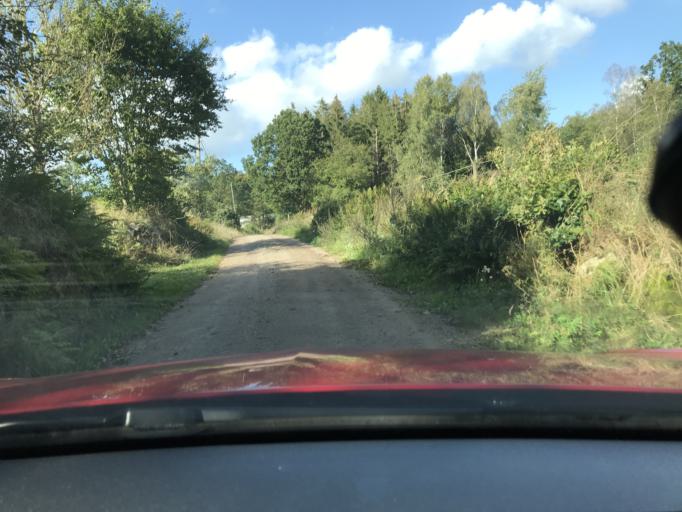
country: SE
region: Skane
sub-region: Hassleholms Kommun
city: Sosdala
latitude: 56.0012
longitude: 13.7046
